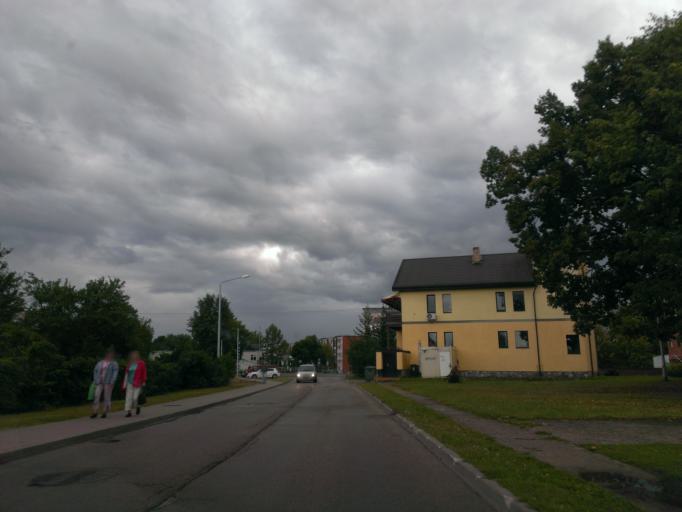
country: LV
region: Salaspils
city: Salaspils
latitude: 56.8537
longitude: 24.3379
